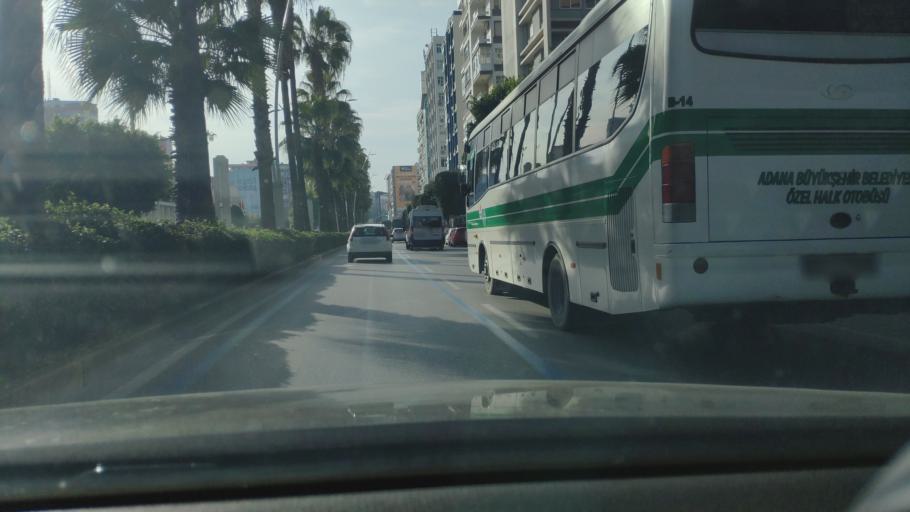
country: TR
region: Adana
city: Adana
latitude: 36.9941
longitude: 35.3251
